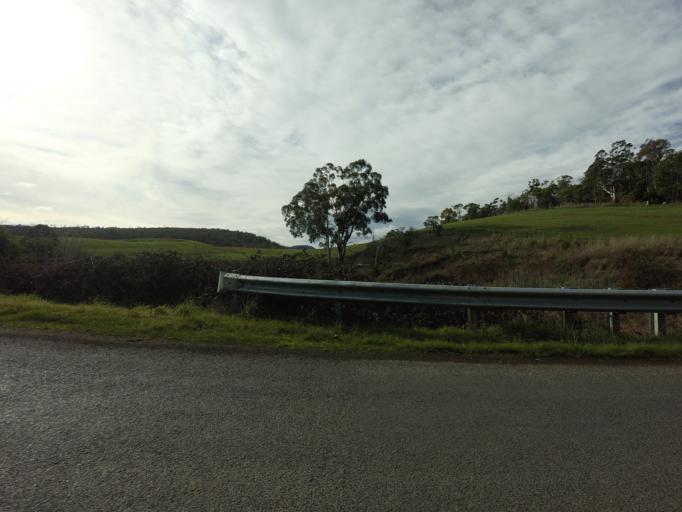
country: AU
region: Tasmania
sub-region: Derwent Valley
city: New Norfolk
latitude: -42.7830
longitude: 146.9944
